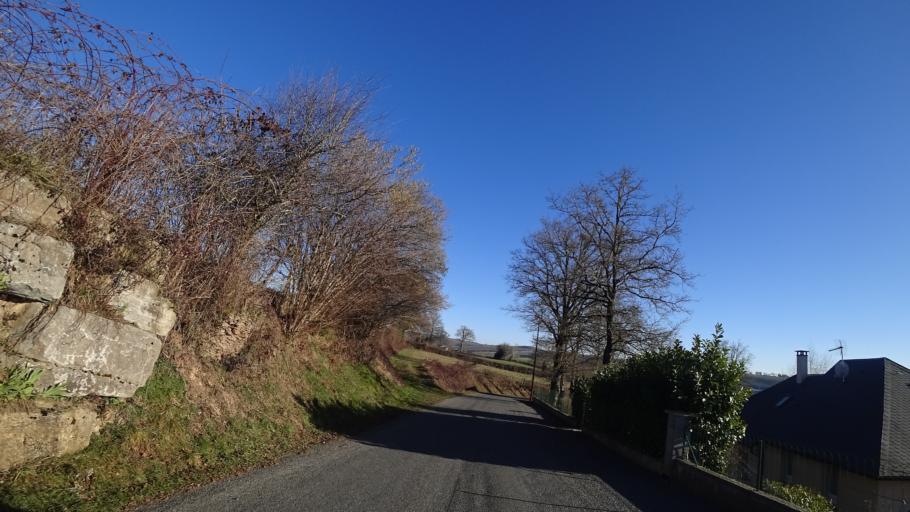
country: FR
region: Midi-Pyrenees
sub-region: Departement de l'Aveyron
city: Pont-de-Salars
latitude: 44.3142
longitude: 2.7584
